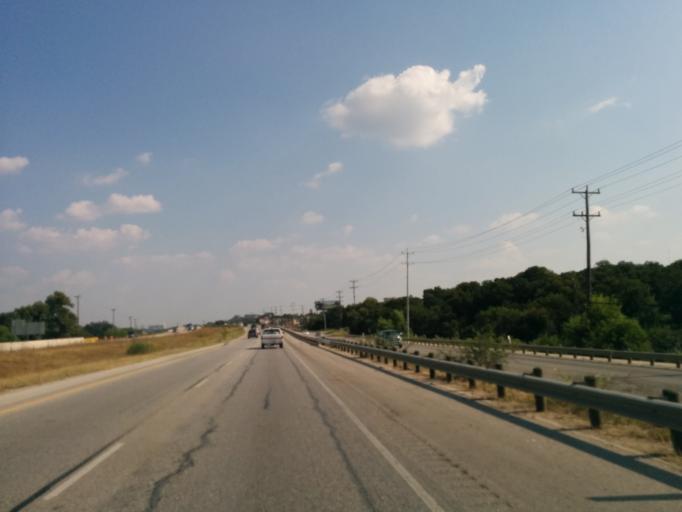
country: US
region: Texas
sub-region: Bexar County
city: Cross Mountain
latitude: 29.6529
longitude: -98.6249
